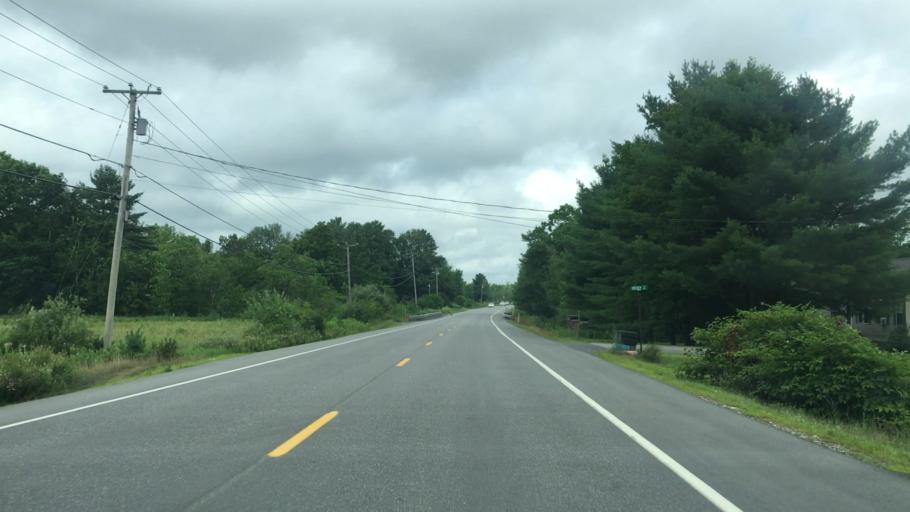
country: US
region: Maine
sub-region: Kennebec County
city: Pittston
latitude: 44.2088
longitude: -69.7547
